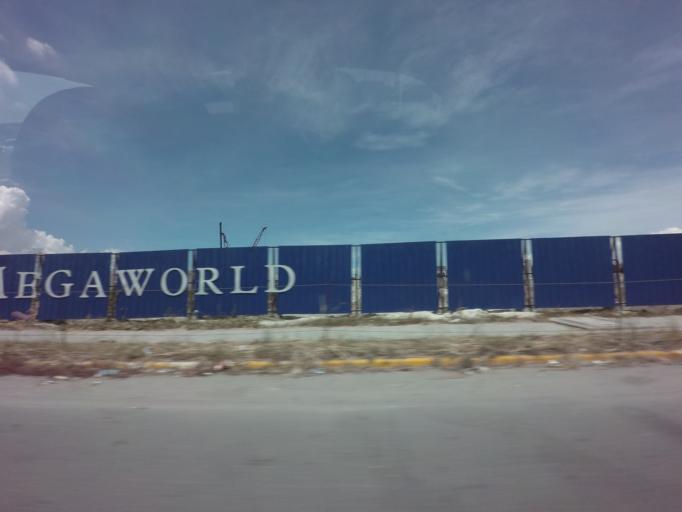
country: PH
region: Metro Manila
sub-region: Makati City
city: Makati City
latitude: 14.5159
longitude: 120.9847
